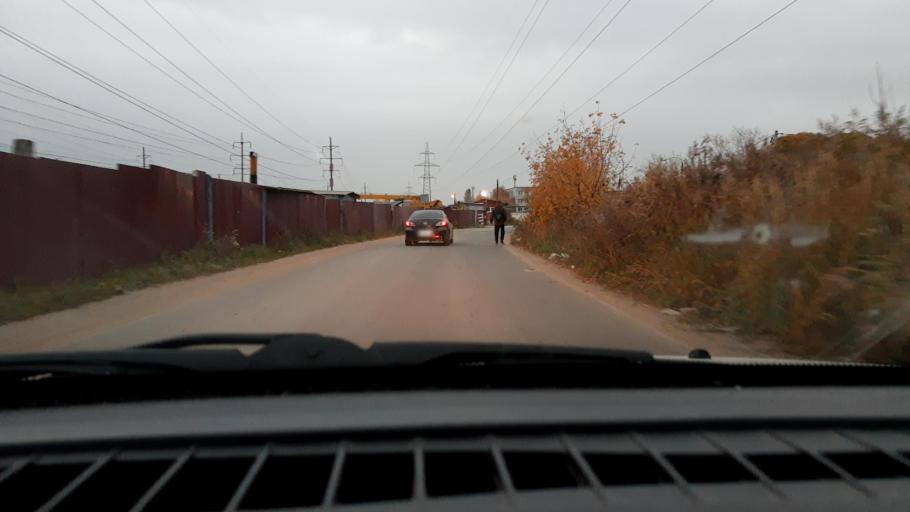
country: RU
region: Nizjnij Novgorod
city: Nizhniy Novgorod
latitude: 56.2780
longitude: 43.8945
